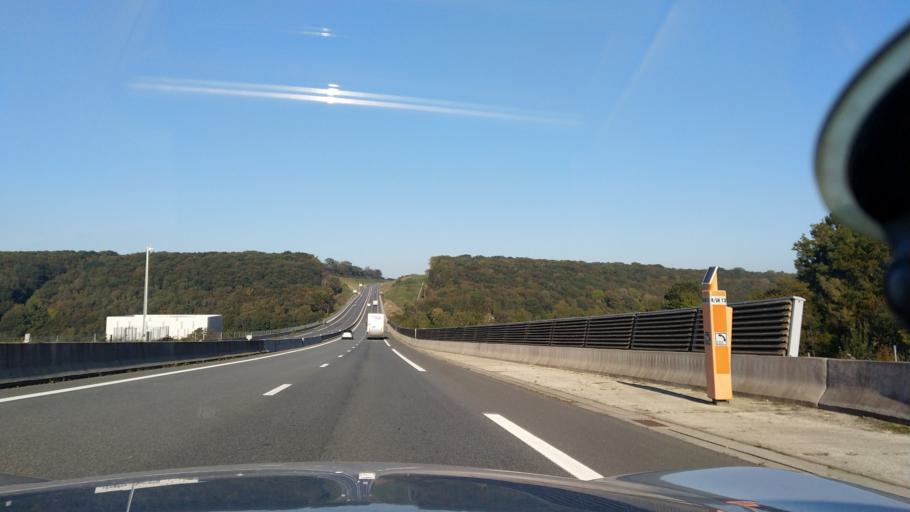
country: FR
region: Haute-Normandie
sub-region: Departement de la Seine-Maritime
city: Barentin
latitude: 49.5313
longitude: 0.9455
